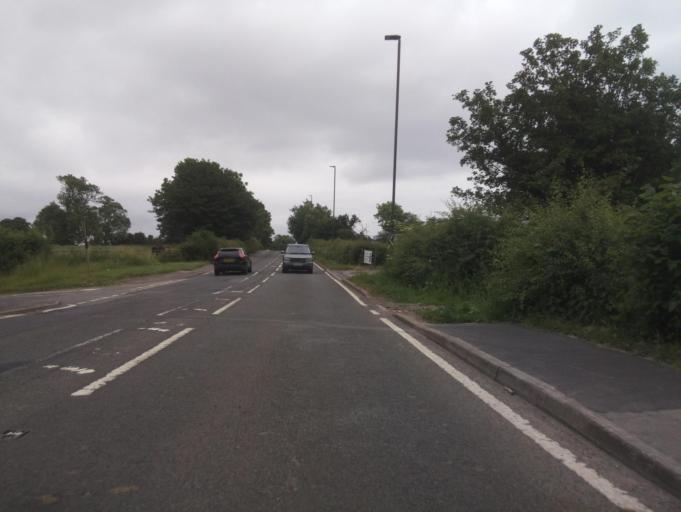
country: GB
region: England
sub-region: Derby
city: Derby
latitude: 52.9368
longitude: -1.5400
